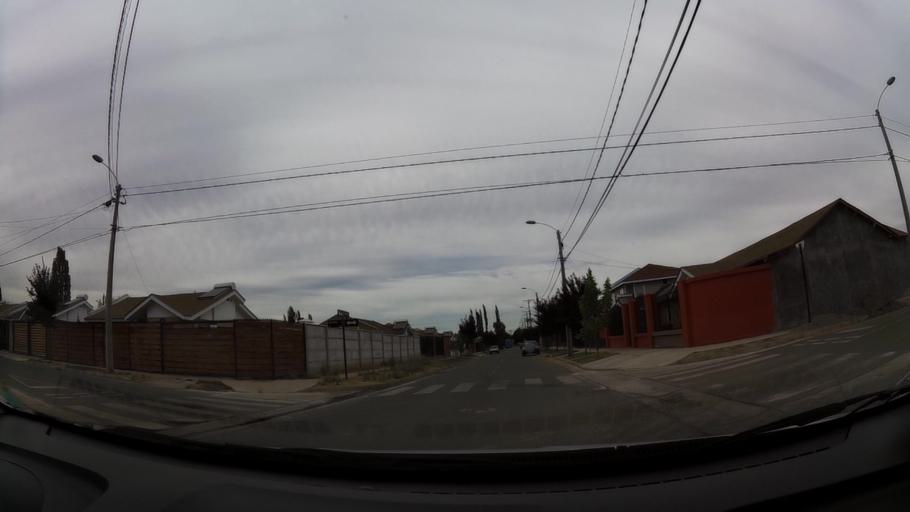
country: CL
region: O'Higgins
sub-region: Provincia de Cachapoal
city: Graneros
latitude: -34.0805
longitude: -70.7375
